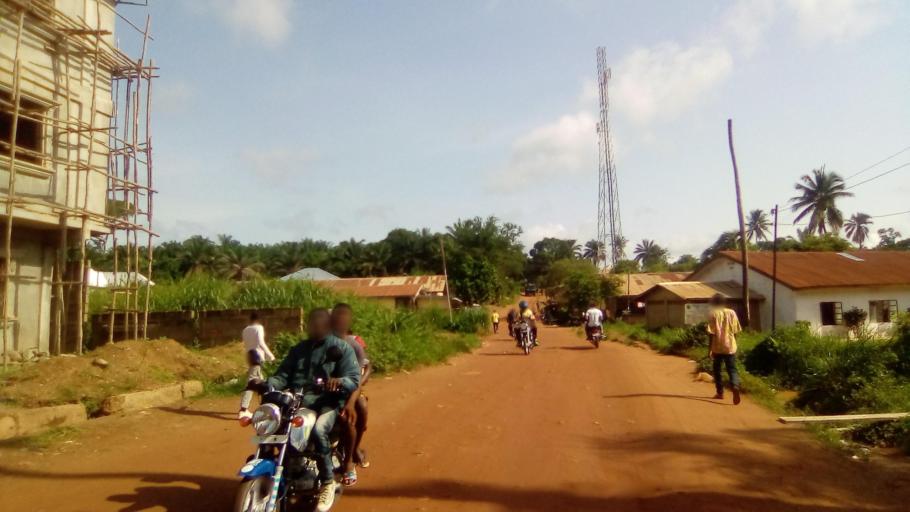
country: SL
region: Southern Province
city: Bo
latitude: 7.9699
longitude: -11.7307
